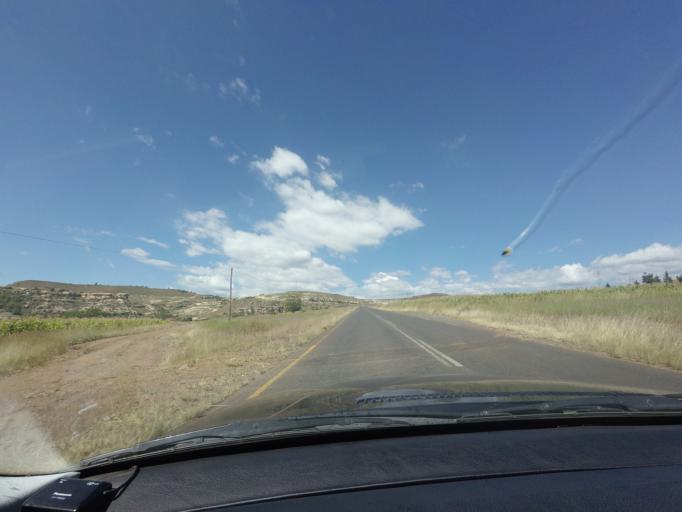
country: LS
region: Butha-Buthe
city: Butha-Buthe
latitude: -28.7147
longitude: 28.3814
